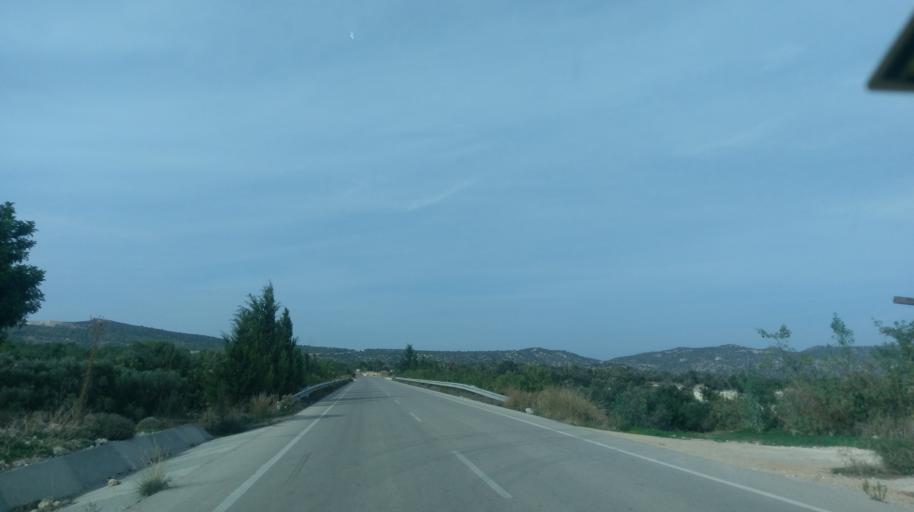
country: CY
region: Ammochostos
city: Trikomo
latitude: 35.4109
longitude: 33.9886
